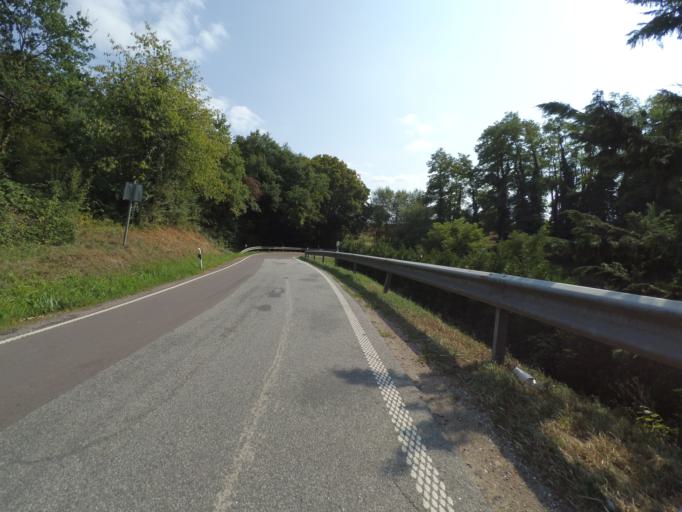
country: LU
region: Grevenmacher
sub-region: Canton de Remich
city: Remich
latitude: 49.5509
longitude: 6.3837
